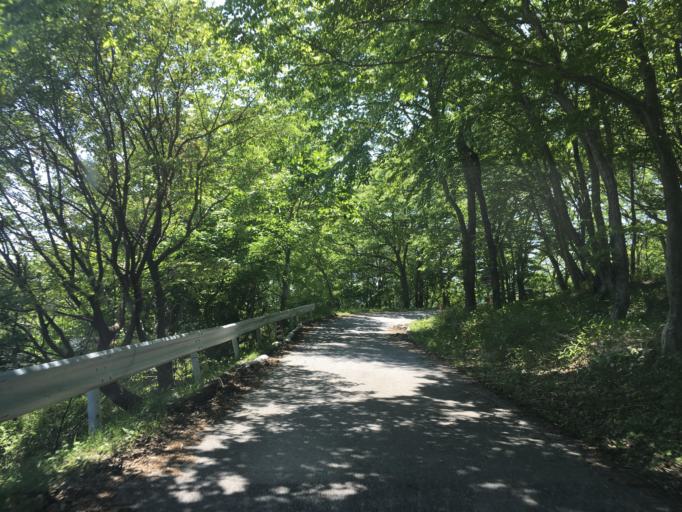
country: JP
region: Iwate
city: Ofunato
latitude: 39.1735
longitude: 141.7294
